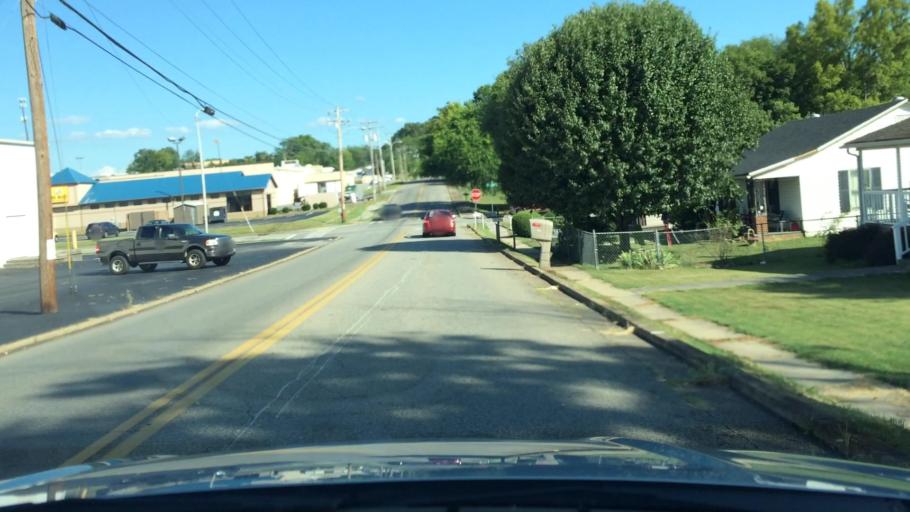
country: US
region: Tennessee
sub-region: Blount County
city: Maryville
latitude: 35.7650
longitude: -83.9735
